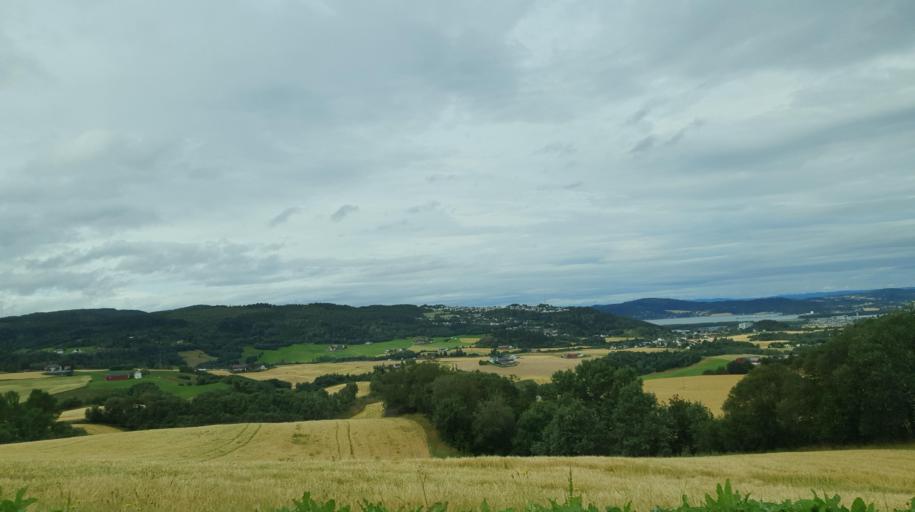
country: NO
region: Nord-Trondelag
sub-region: Stjordal
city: Stjordalshalsen
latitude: 63.4246
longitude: 10.9569
